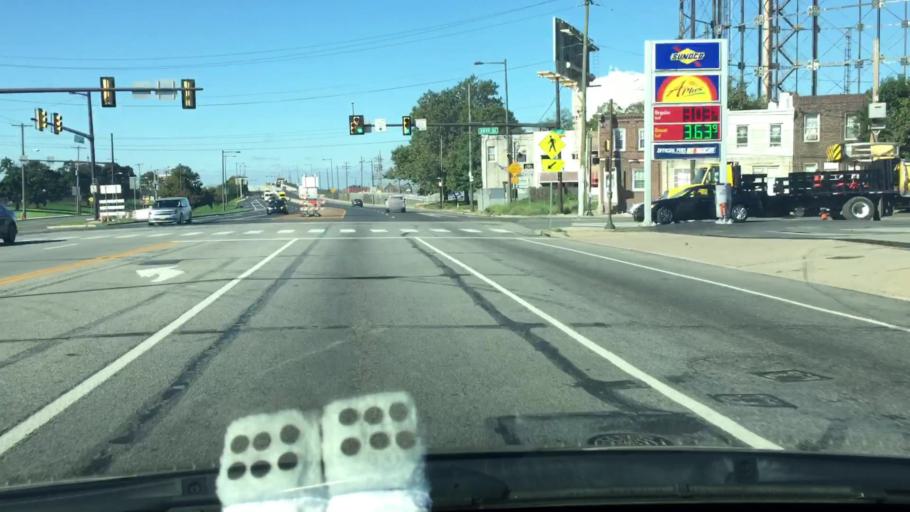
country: US
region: Pennsylvania
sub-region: Philadelphia County
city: Philadelphia
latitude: 39.9212
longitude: -75.1932
